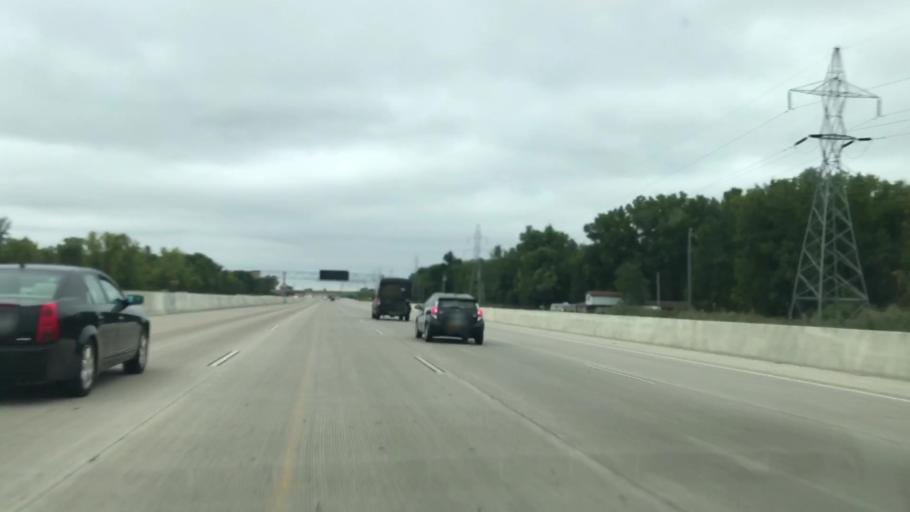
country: US
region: Wisconsin
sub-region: Brown County
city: Suamico
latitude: 44.5846
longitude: -88.0487
